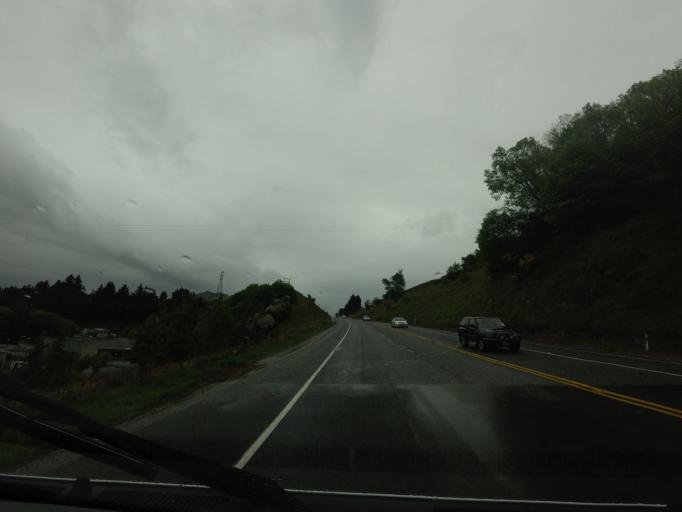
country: NZ
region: Otago
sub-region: Queenstown-Lakes District
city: Arrowtown
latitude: -45.0027
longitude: 168.7543
